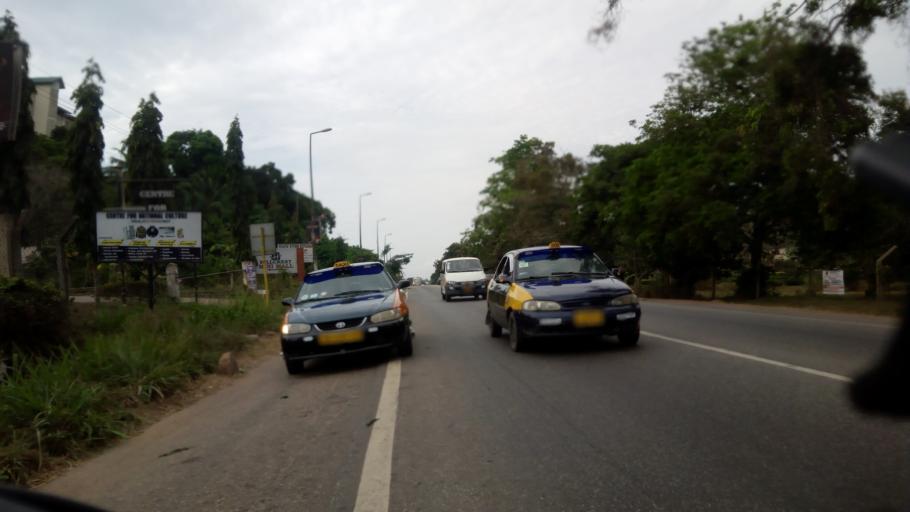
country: GH
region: Central
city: Cape Coast
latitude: 5.1118
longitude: -1.2791
